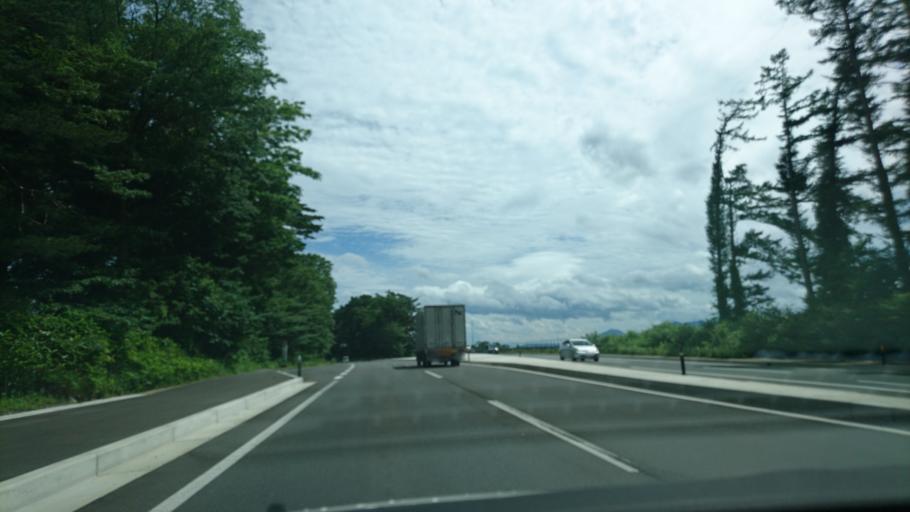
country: JP
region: Iwate
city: Morioka-shi
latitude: 39.7672
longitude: 141.1312
